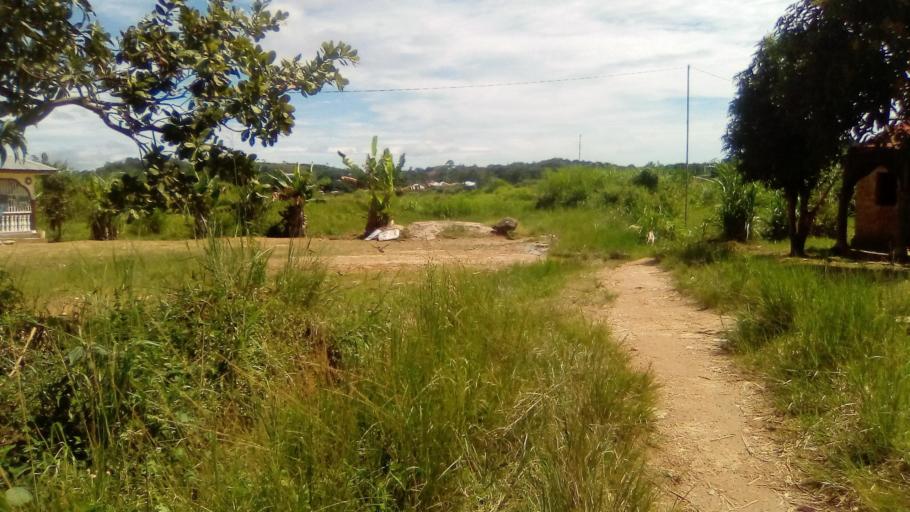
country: SL
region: Eastern Province
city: Koidu
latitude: 8.6374
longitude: -10.9922
